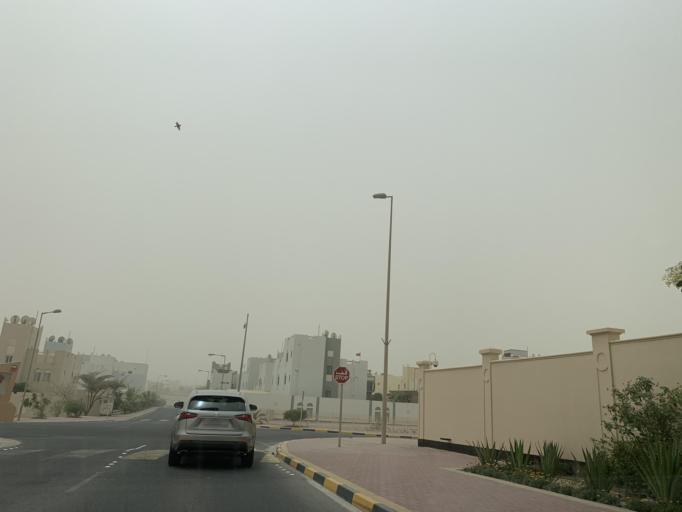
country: BH
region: Central Governorate
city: Madinat Hamad
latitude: 26.1362
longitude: 50.5148
